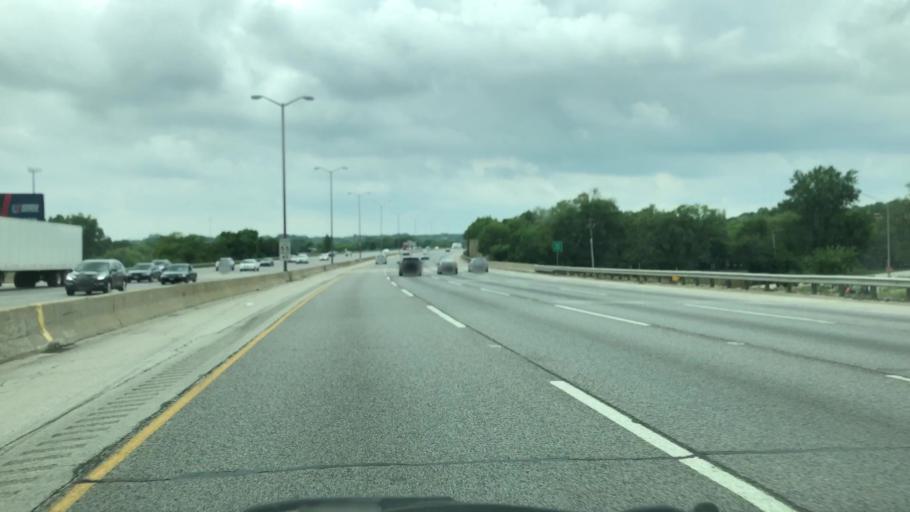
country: US
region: Illinois
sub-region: Cook County
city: Indian Head Park
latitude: 41.7619
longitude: -87.8956
